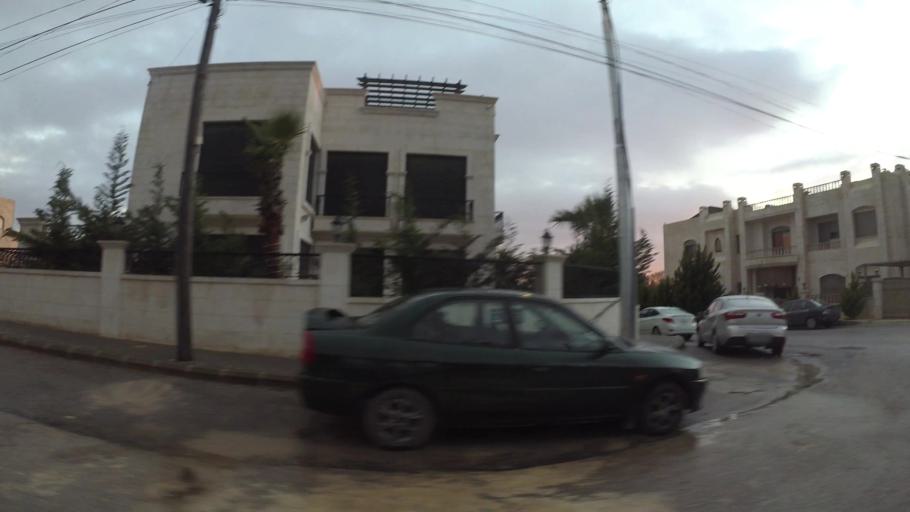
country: JO
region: Amman
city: Al Jubayhah
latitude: 32.0337
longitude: 35.8176
